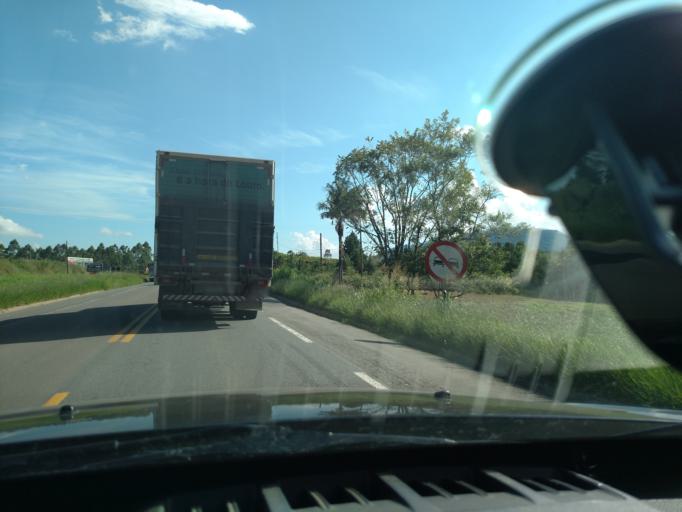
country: BR
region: Santa Catarina
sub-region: Ibirama
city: Ibirama
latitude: -27.1188
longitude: -49.5340
